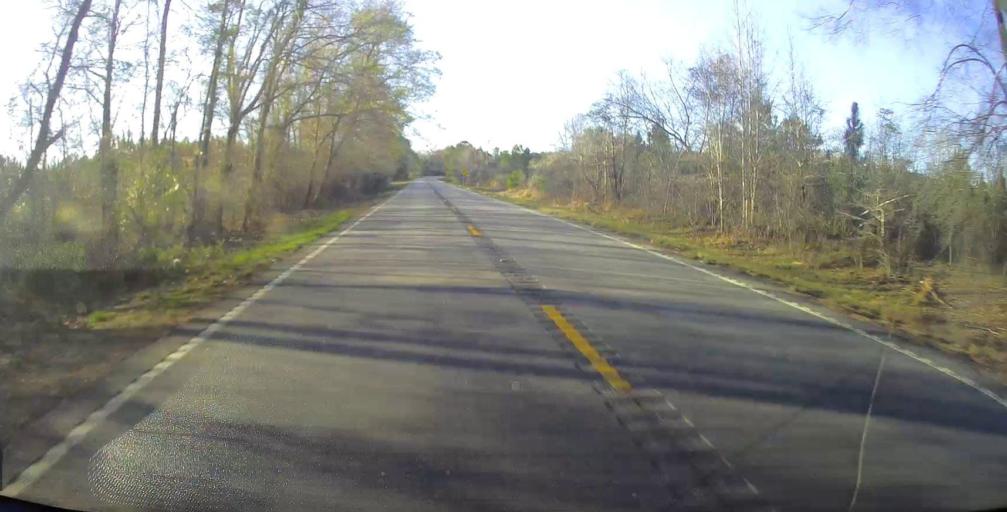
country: US
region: Georgia
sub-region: Wilcox County
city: Abbeville
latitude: 32.1202
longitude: -83.3274
